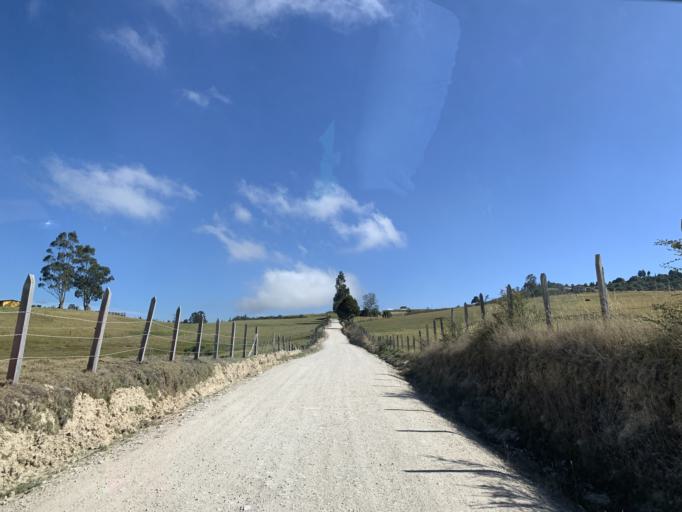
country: CO
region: Boyaca
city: Tuta
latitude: 5.6843
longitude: -73.1460
